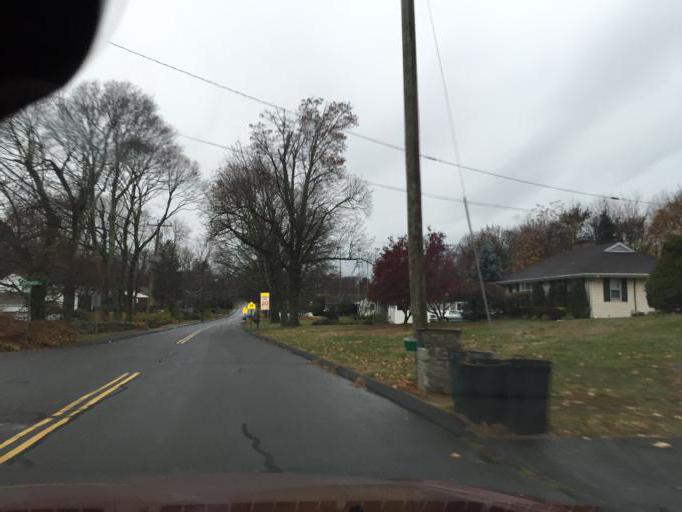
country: US
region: Connecticut
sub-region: Fairfield County
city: East Norwalk
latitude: 41.1169
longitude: -73.3902
